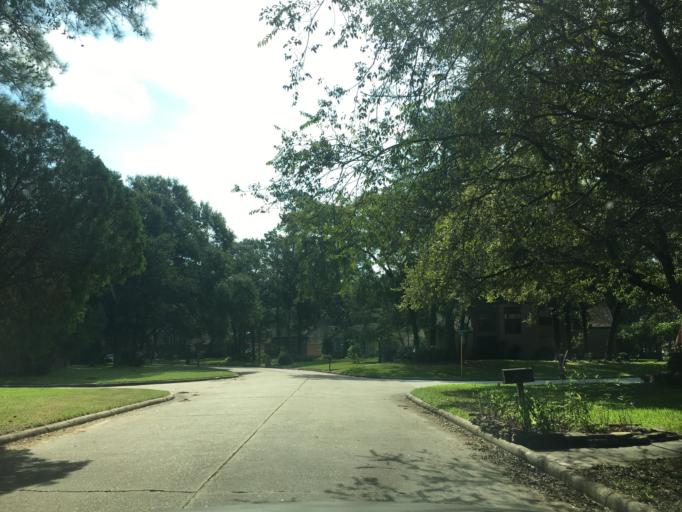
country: US
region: Texas
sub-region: Harris County
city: Spring
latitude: 30.0504
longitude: -95.4435
